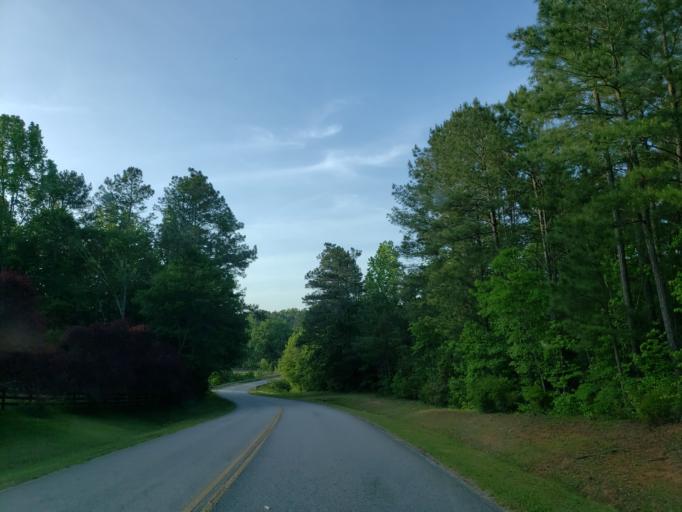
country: US
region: Georgia
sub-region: Carroll County
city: Mount Zion
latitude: 33.6416
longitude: -85.1871
